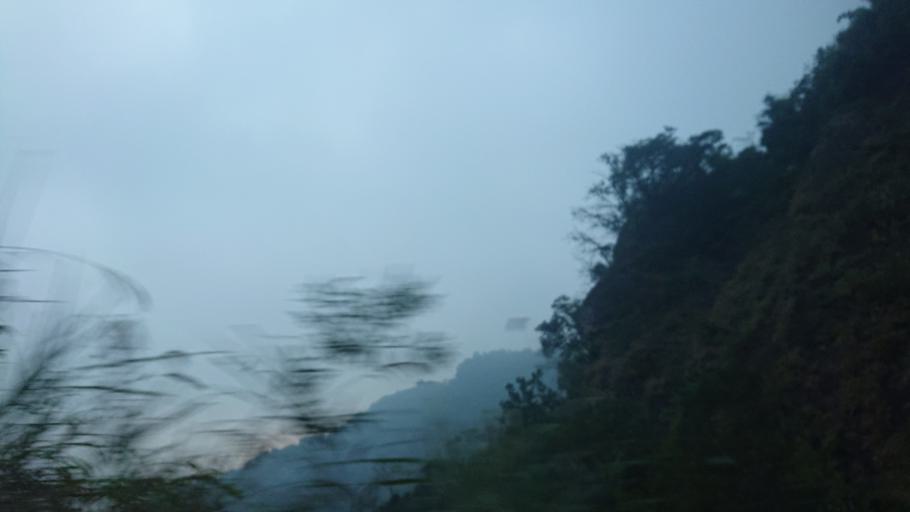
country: TW
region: Taiwan
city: Lugu
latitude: 23.5961
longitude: 120.7240
